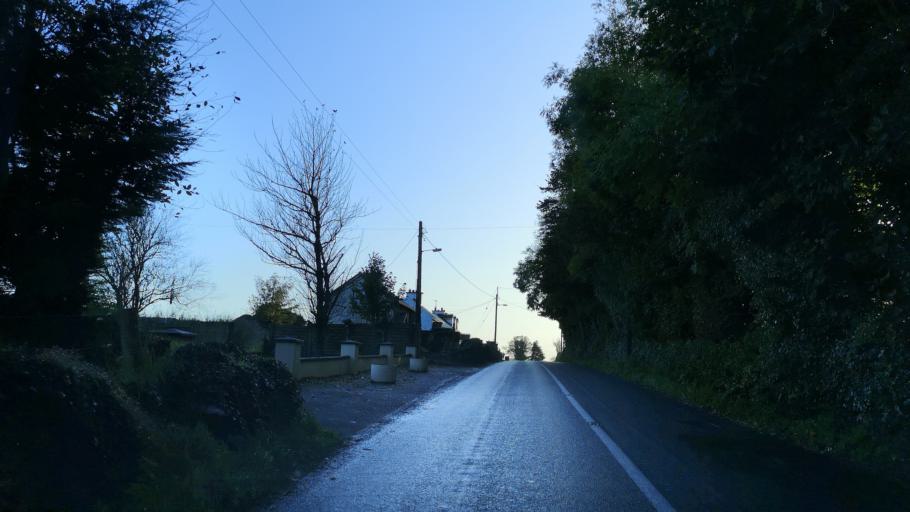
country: IE
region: Connaught
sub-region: Roscommon
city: Castlerea
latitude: 53.7638
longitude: -8.5062
